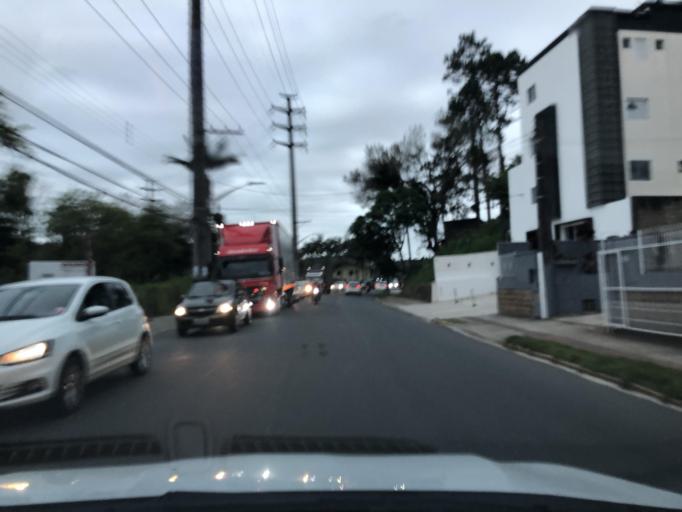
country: BR
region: Santa Catarina
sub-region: Joinville
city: Joinville
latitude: -26.2933
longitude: -48.8765
